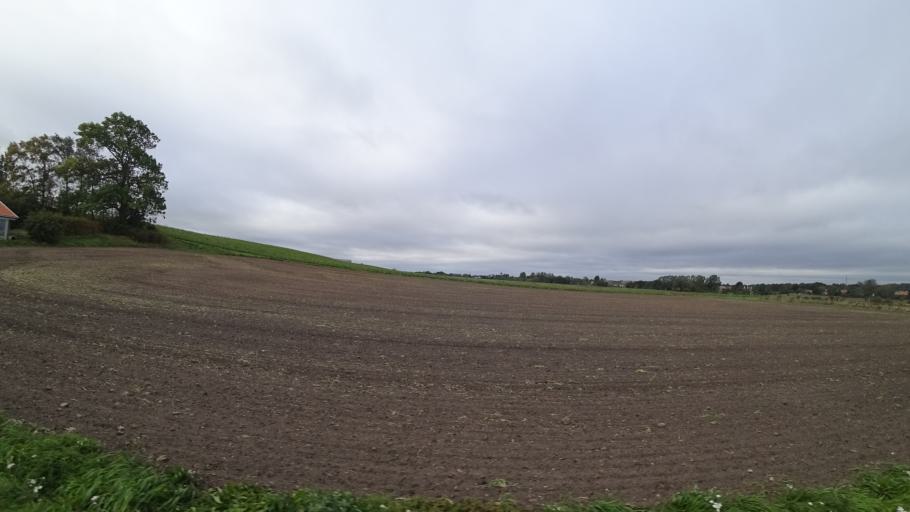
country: SE
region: Skane
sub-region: Kavlinge Kommun
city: Kaevlinge
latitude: 55.7891
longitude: 13.1382
